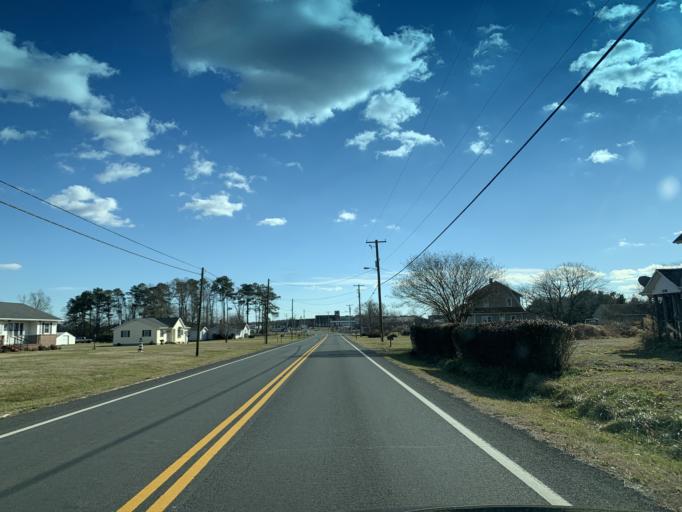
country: US
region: Maryland
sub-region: Worcester County
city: Berlin
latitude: 38.3465
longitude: -75.1917
